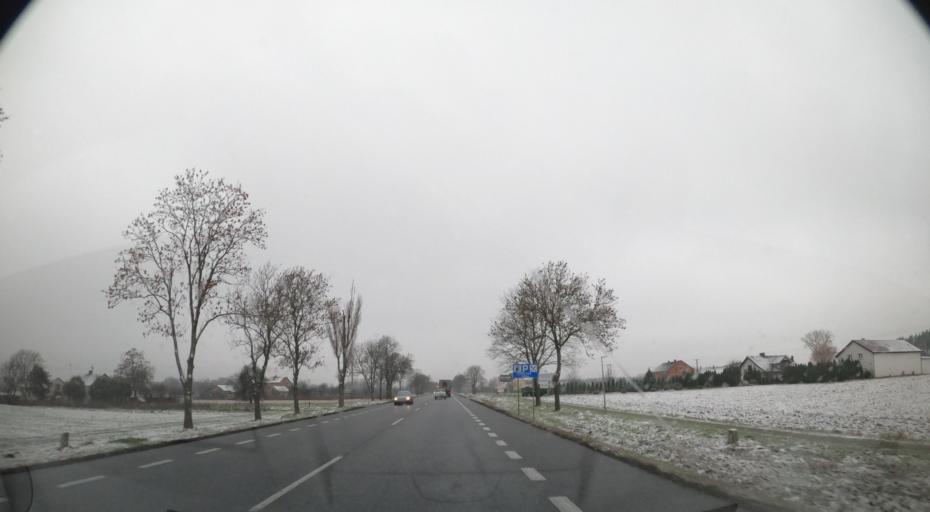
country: PL
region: Masovian Voivodeship
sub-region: Powiat sochaczewski
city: Sochaczew
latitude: 52.2219
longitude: 20.3218
